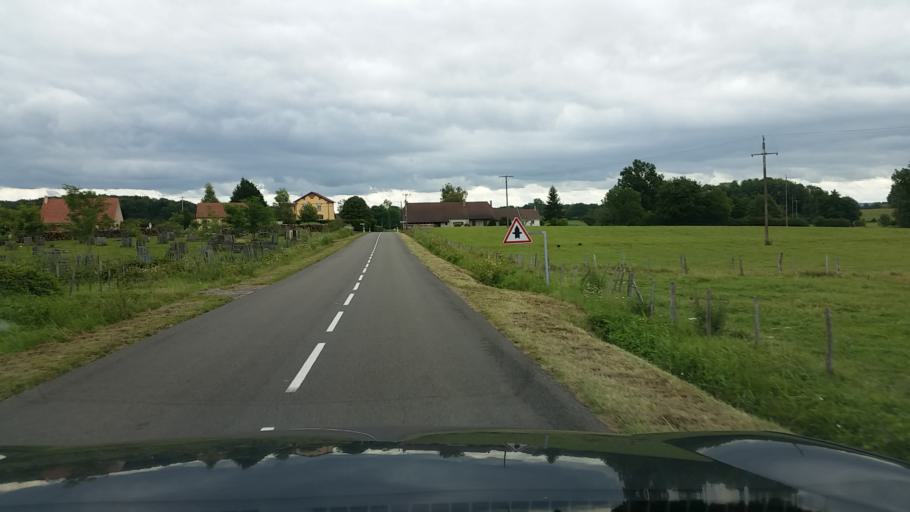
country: FR
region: Bourgogne
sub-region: Departement de Saone-et-Loire
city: Saint-Usuge
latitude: 46.7080
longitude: 5.3329
